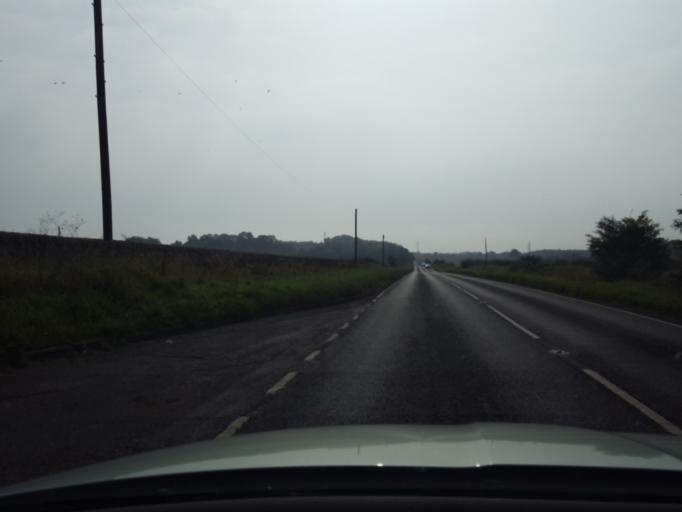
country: GB
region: Scotland
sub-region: Fife
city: Crossgates
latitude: 56.0680
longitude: -3.3752
